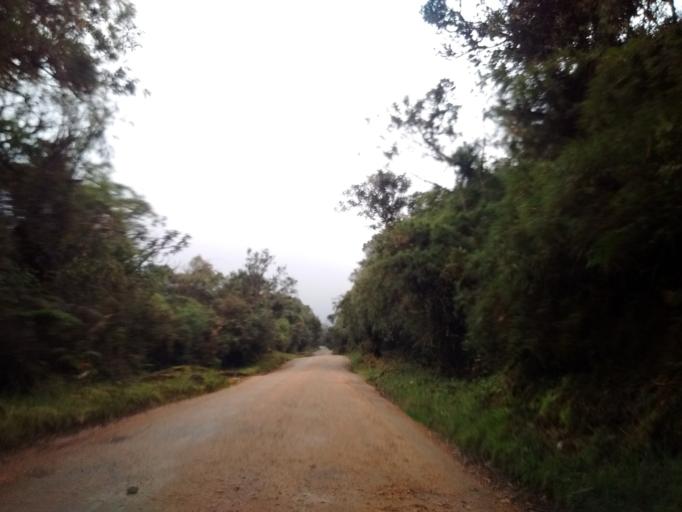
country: CO
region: Huila
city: Isnos
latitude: 2.1187
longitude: -76.3763
